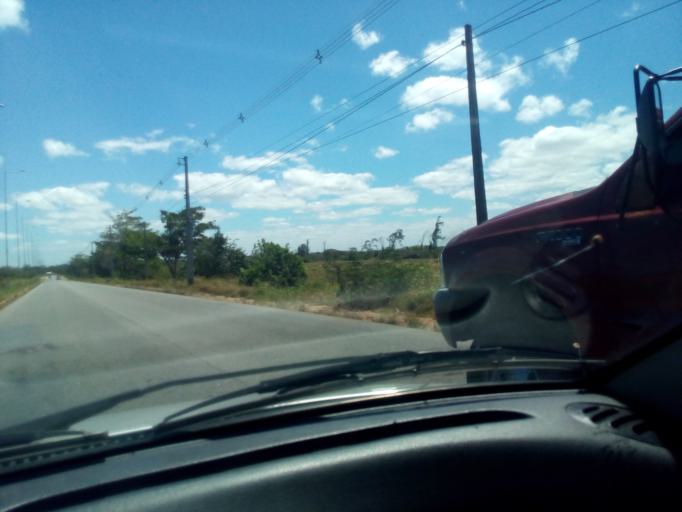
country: BR
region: Rio Grande do Norte
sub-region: Sao Goncalo Do Amarante
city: Sao Goncalo do Amarante
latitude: -5.8036
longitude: -35.3288
